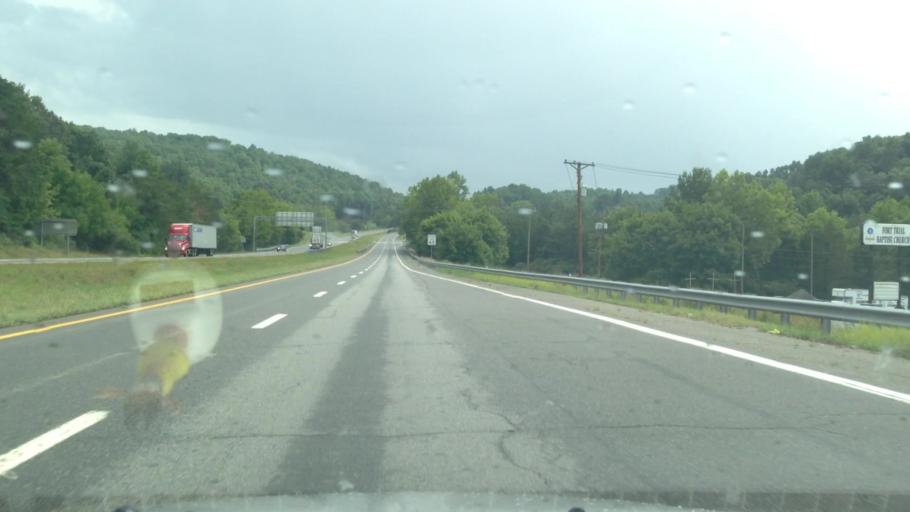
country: US
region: Virginia
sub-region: Henry County
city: Stanleytown
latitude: 36.7335
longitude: -79.9376
